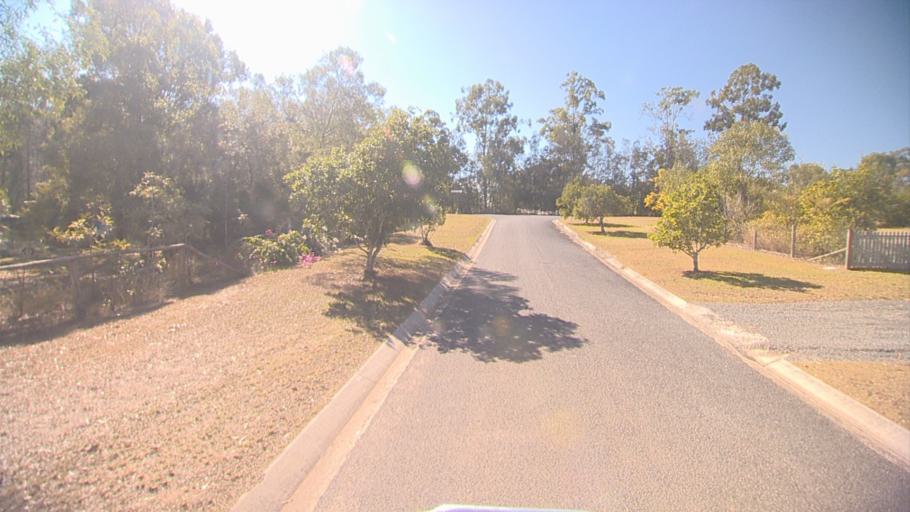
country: AU
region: Queensland
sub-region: Logan
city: North Maclean
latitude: -27.8246
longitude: 152.9420
